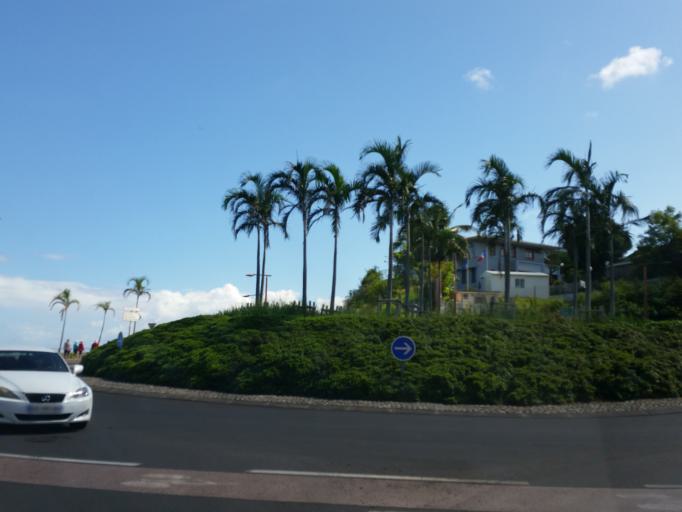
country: RE
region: Reunion
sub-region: Reunion
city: Sainte-Marie
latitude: -20.8957
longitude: 55.5516
